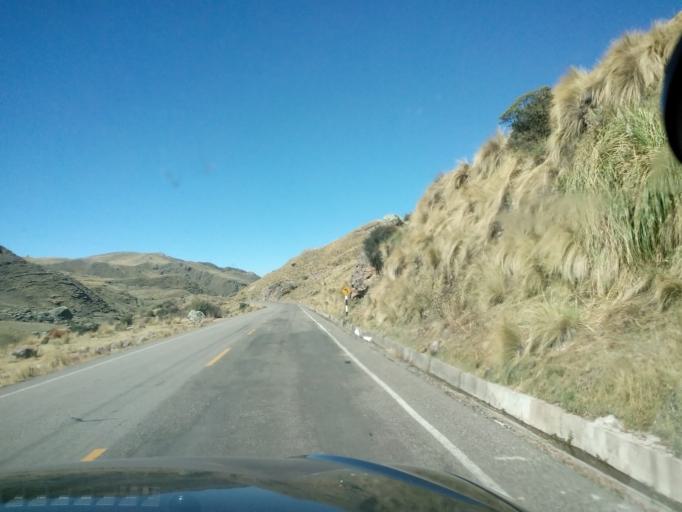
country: PE
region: Ayacucho
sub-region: Provincia de Cangallo
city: Totos
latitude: -13.3432
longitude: -74.5572
